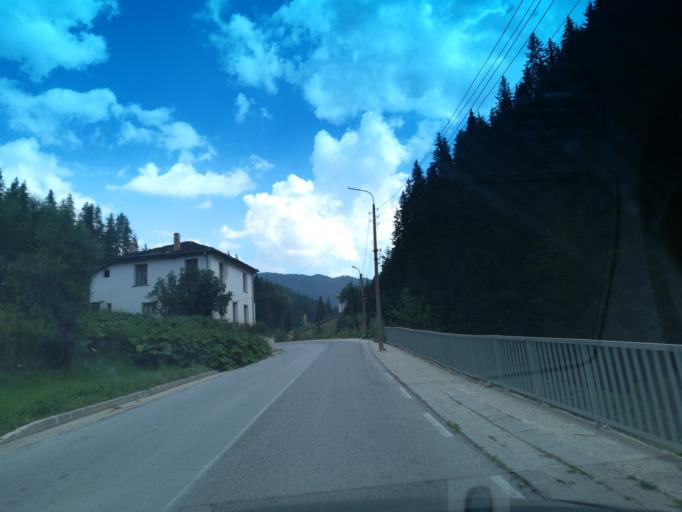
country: BG
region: Smolyan
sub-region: Obshtina Smolyan
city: Smolyan
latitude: 41.6559
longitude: 24.6343
